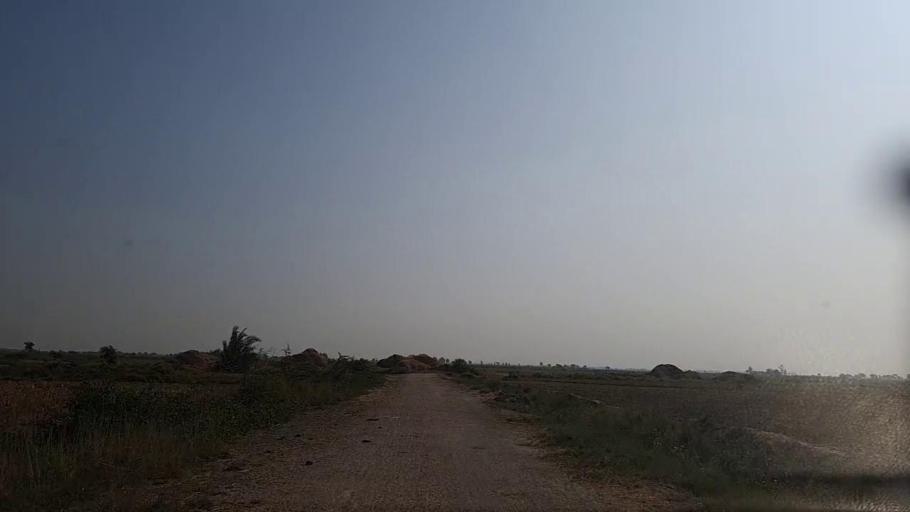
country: PK
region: Sindh
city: Mirpur Batoro
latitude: 24.5784
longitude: 68.2252
